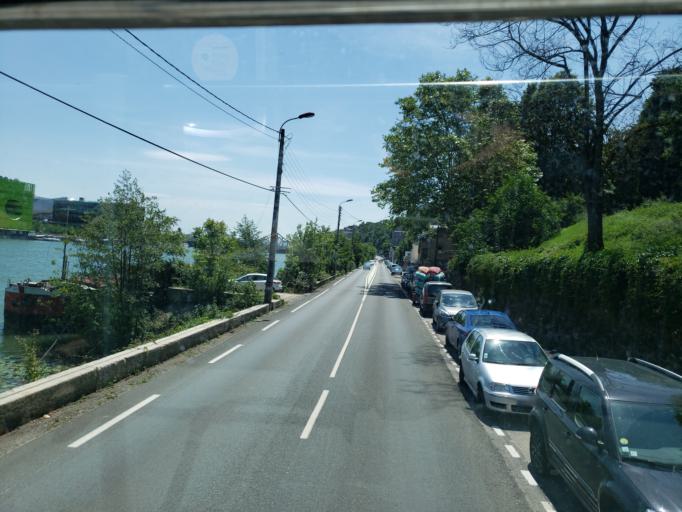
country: FR
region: Rhone-Alpes
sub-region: Departement du Rhone
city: La Mulatiere
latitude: 45.7367
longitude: 4.8120
